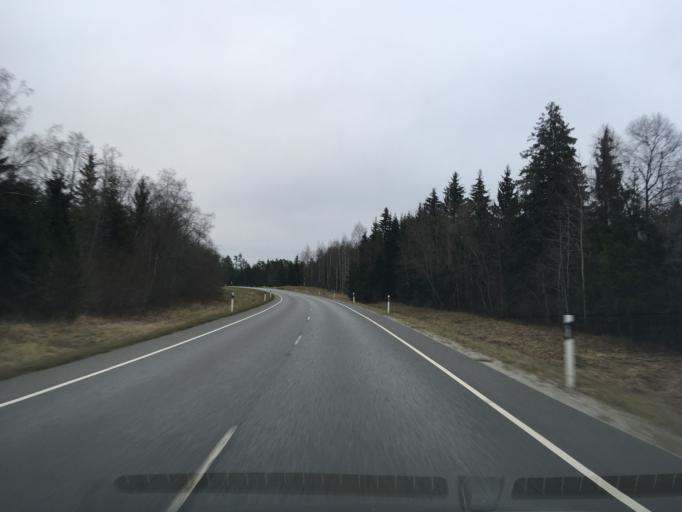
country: EE
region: Laeaene-Virumaa
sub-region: Kadrina vald
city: Kadrina
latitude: 59.4482
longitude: 26.0649
